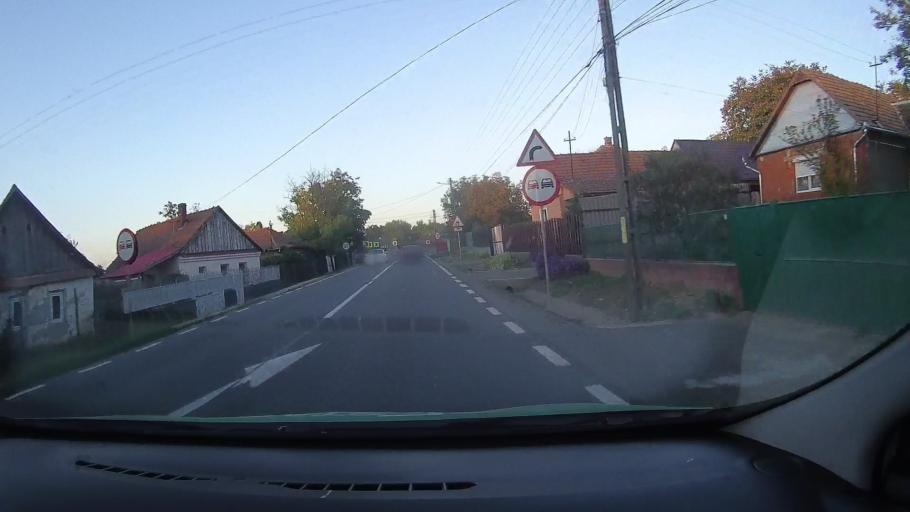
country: RO
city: Szekelyhid
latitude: 47.3351
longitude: 22.0874
